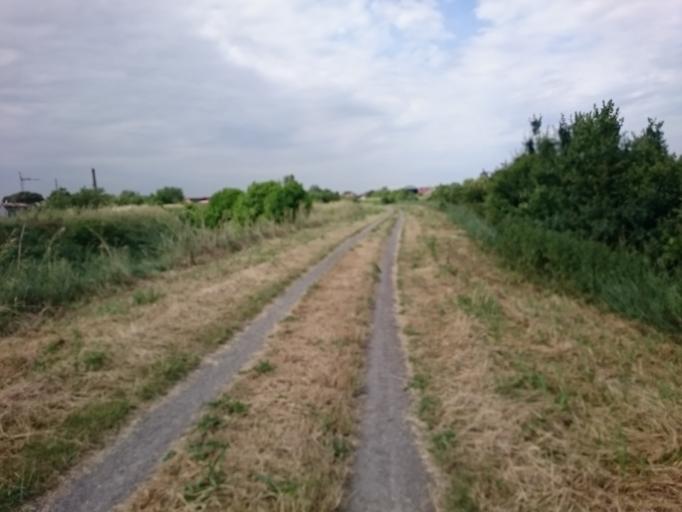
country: IT
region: Veneto
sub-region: Provincia di Padova
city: Este
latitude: 45.2230
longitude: 11.6800
